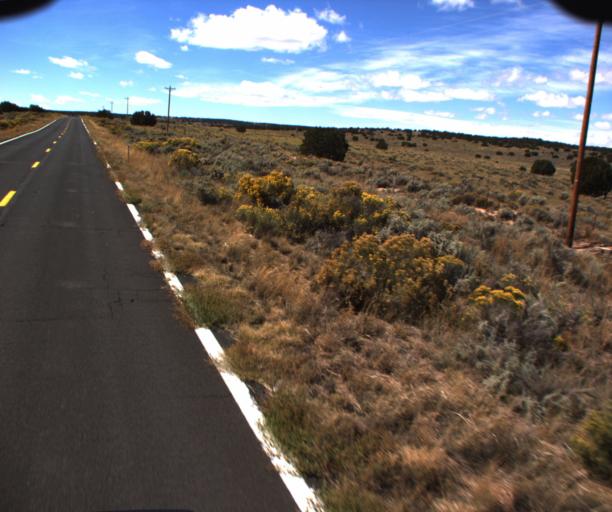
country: US
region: New Mexico
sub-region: McKinley County
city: Zuni Pueblo
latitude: 35.0016
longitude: -109.0867
